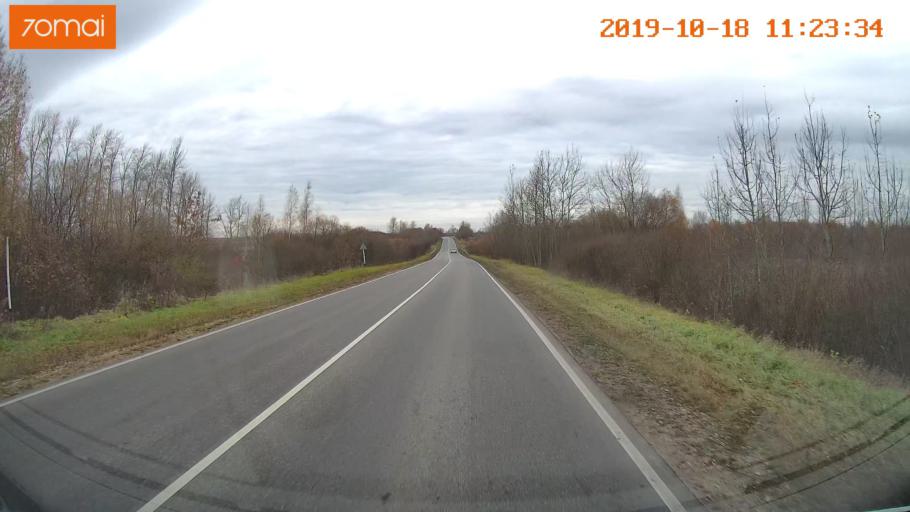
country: RU
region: Tula
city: Kimovsk
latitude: 54.1033
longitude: 38.5949
